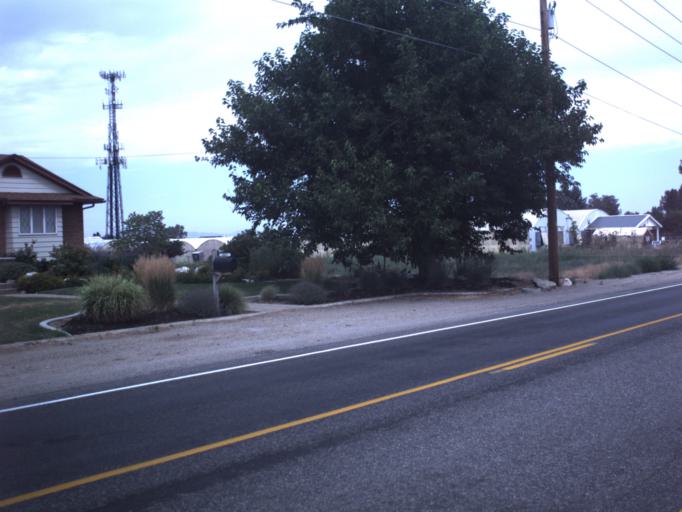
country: US
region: Utah
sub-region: Davis County
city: Clinton
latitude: 41.1283
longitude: -112.0645
